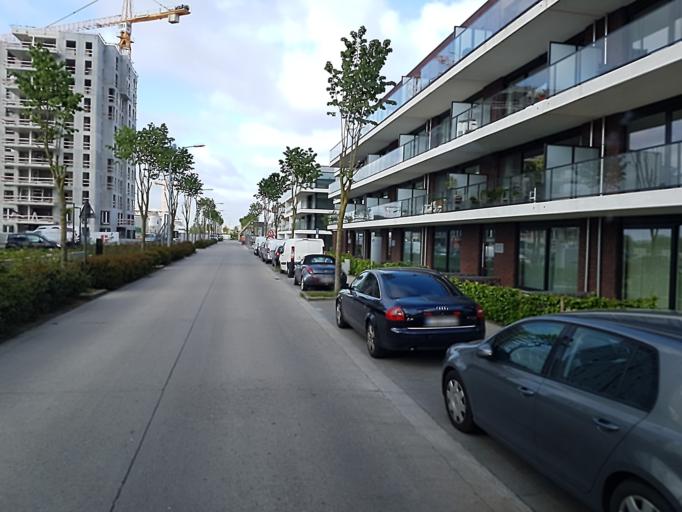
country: BE
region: Flanders
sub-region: Provincie Oost-Vlaanderen
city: Temse
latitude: 51.1219
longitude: 4.2067
